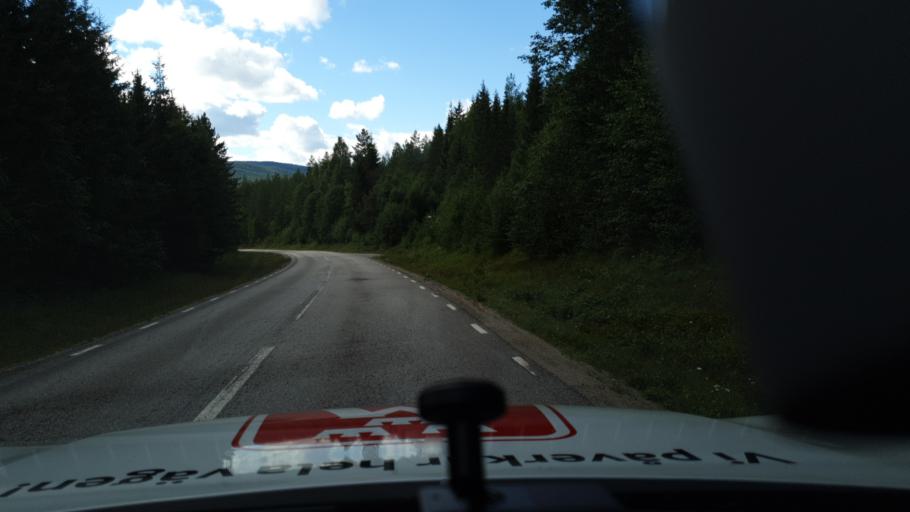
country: NO
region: Hedmark
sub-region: Trysil
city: Innbygda
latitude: 61.0299
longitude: 12.4826
